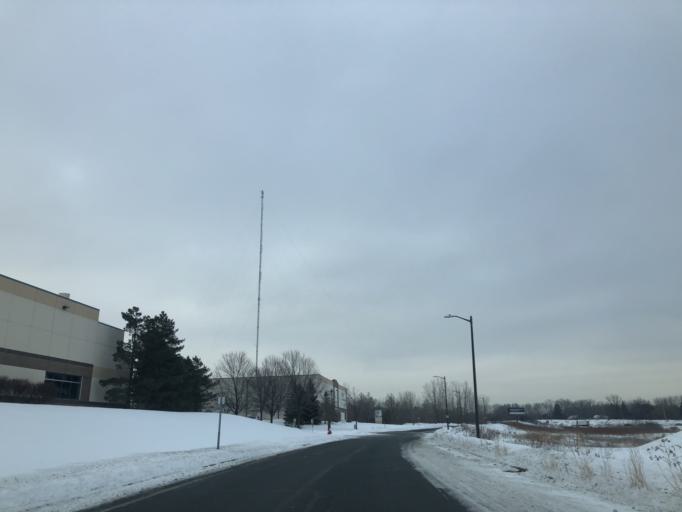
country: US
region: Minnesota
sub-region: Ramsey County
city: New Brighton
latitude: 45.0701
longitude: -93.1817
